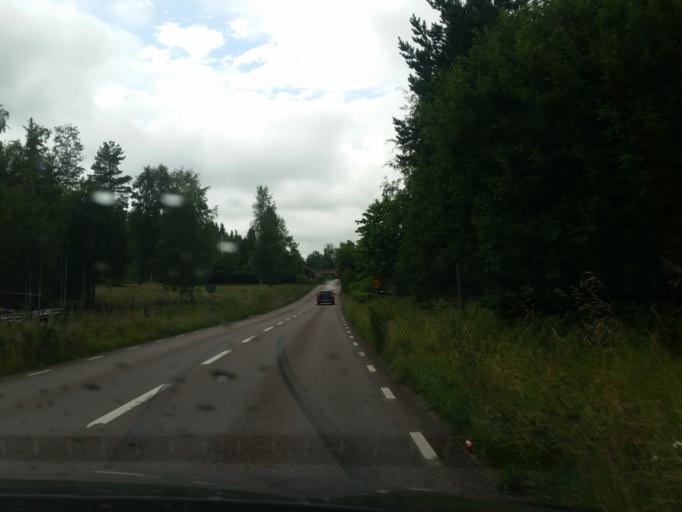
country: SE
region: Dalarna
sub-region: Leksand Municipality
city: Leksand
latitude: 60.7155
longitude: 14.9727
